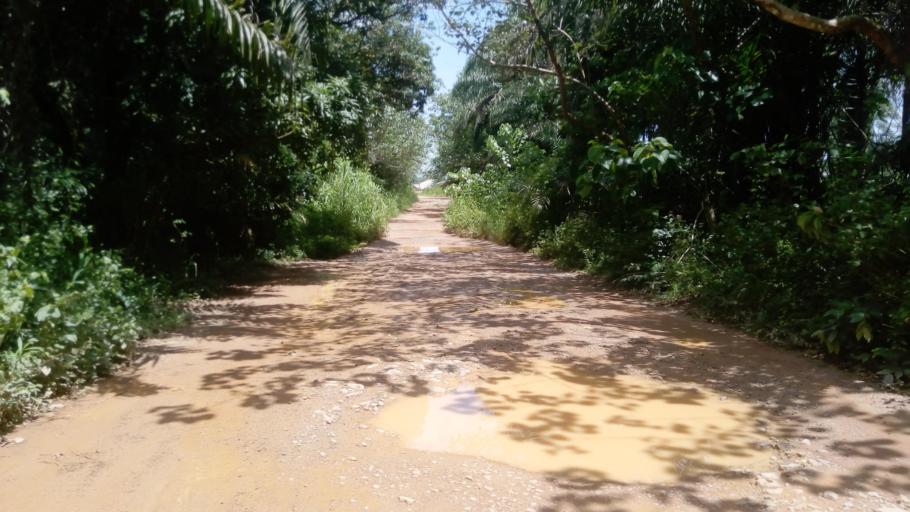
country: SL
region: Northern Province
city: Binkolo
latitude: 8.9534
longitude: -11.9731
